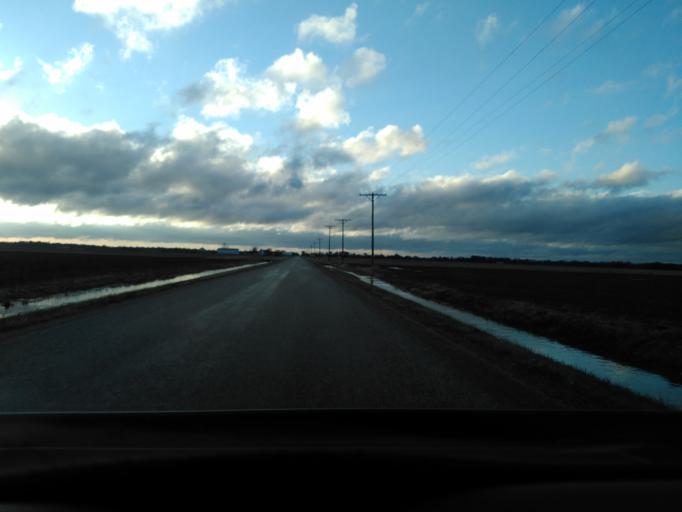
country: US
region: Illinois
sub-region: Effingham County
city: Altamont
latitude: 38.9577
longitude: -88.7285
